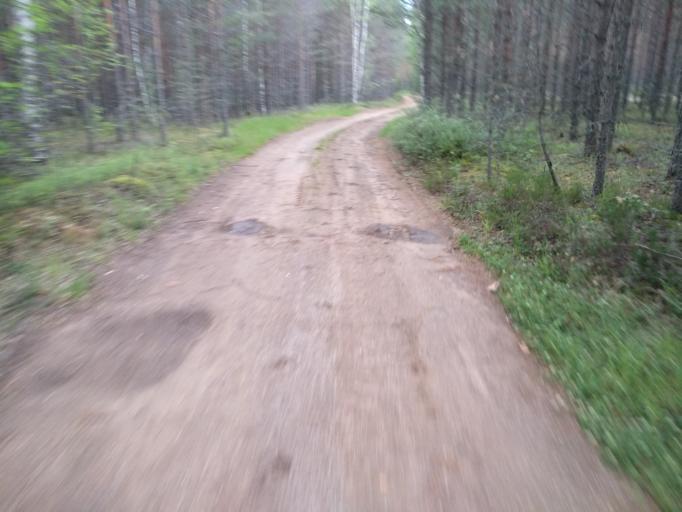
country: RU
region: Tverskaya
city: Krasnomayskiy
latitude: 57.5354
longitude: 34.2965
